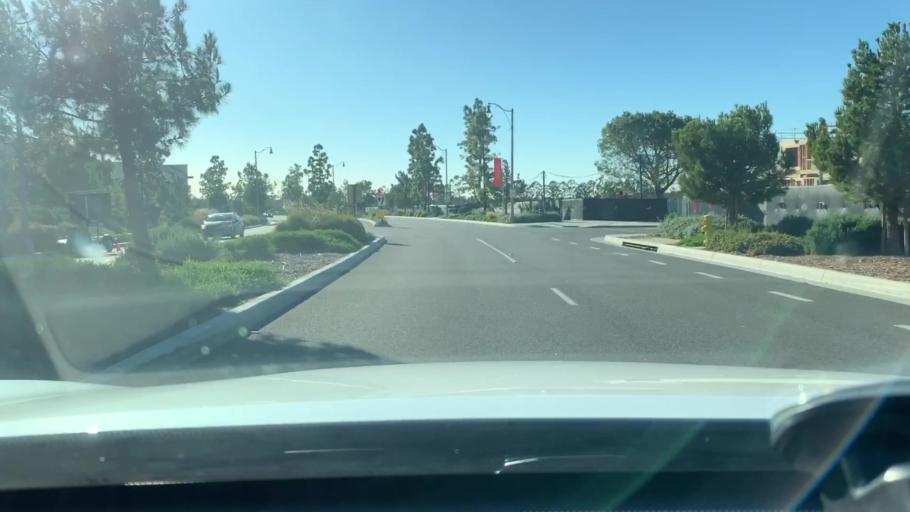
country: US
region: California
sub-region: Orange County
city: Lake Forest
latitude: 33.6921
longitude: -117.7351
